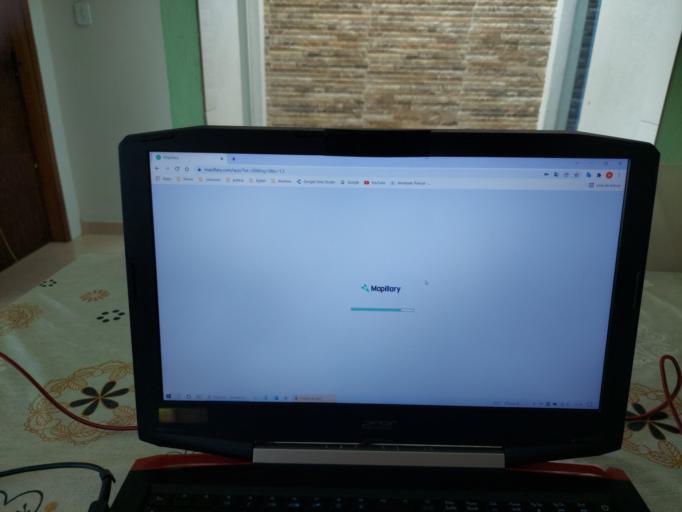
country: BR
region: Alagoas
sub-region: Igreja Nova
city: Igreja Nova
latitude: -10.1299
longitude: -36.6535
